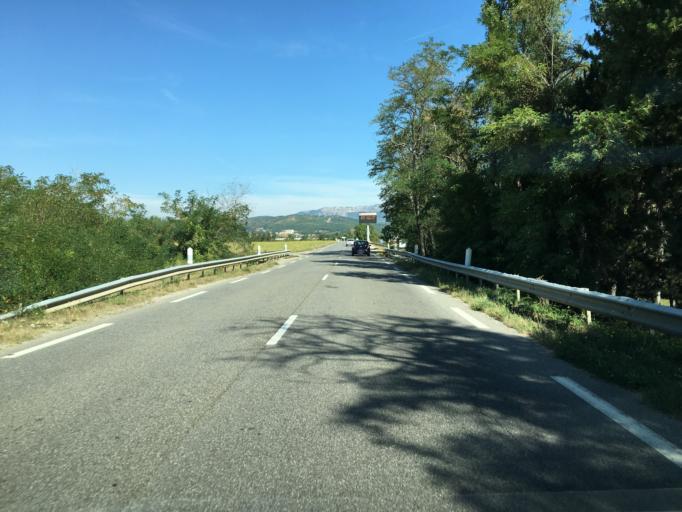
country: FR
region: Provence-Alpes-Cote d'Azur
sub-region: Departement des Hautes-Alpes
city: Laragne-Monteglin
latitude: 44.2945
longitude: 5.8417
